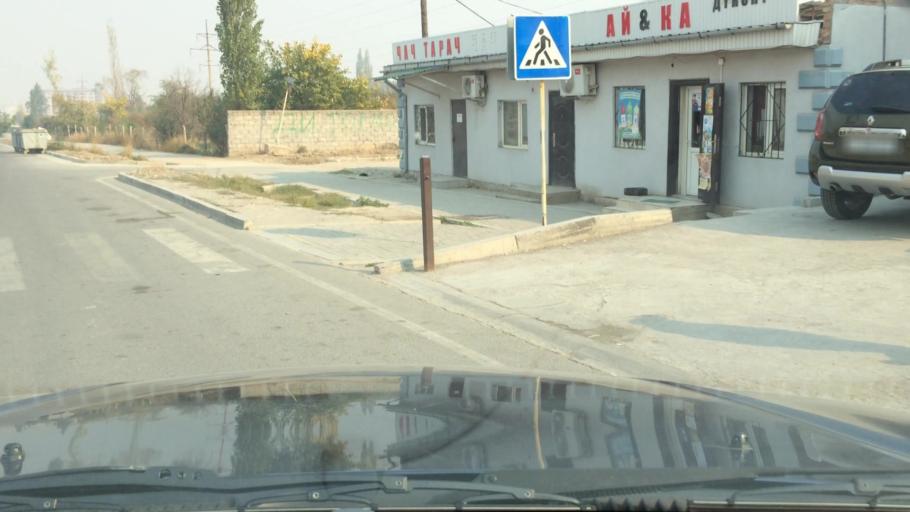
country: KG
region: Chuy
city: Bishkek
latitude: 42.8221
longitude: 74.5700
